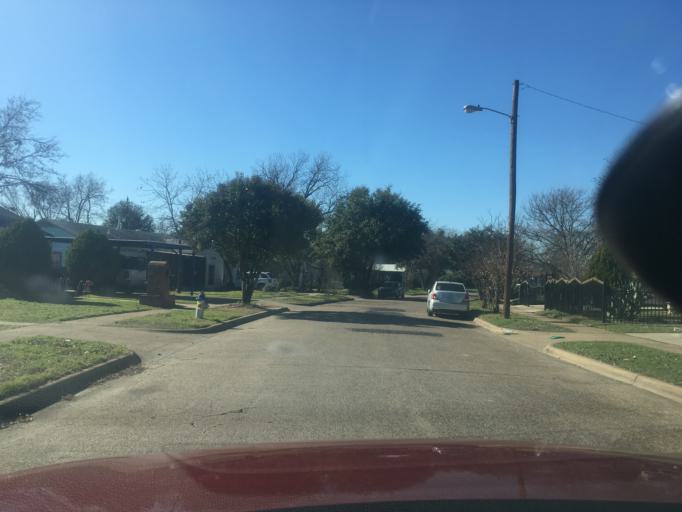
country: US
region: Texas
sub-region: Dallas County
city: Cockrell Hill
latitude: 32.7057
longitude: -96.8332
